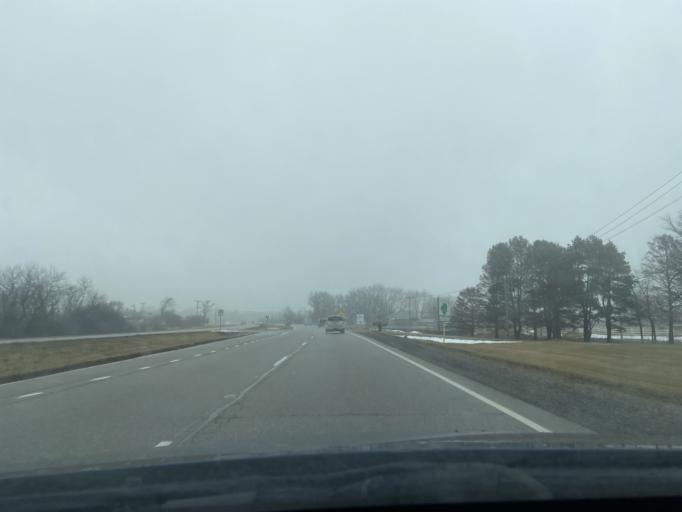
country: US
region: Illinois
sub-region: Lake County
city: Volo
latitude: 42.2914
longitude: -88.1589
